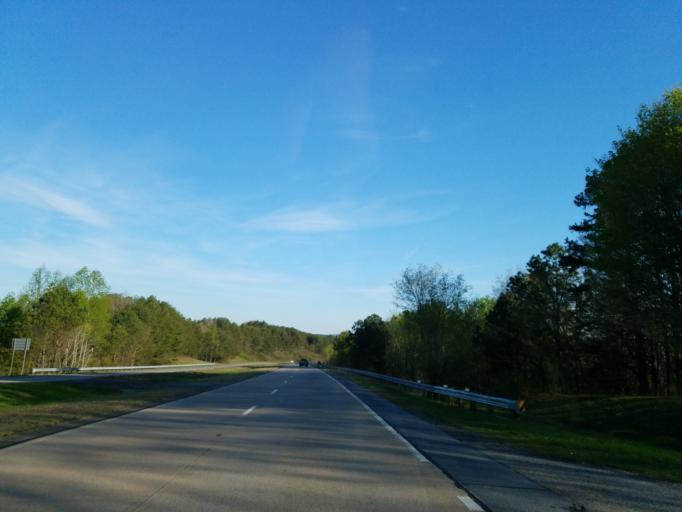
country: US
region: Georgia
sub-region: Pickens County
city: Jasper
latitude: 34.5419
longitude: -84.5177
